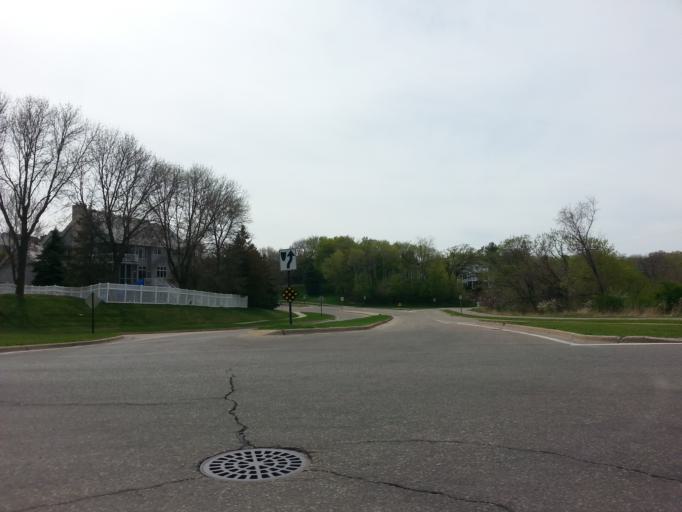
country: US
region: Minnesota
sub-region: Scott County
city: Savage
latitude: 44.8276
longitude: -93.3798
